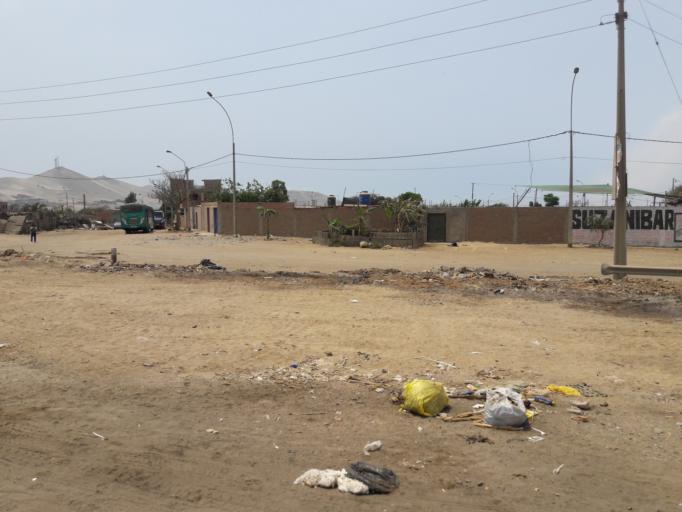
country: PE
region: Lima
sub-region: Lima
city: Santa Rosa
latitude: -11.7732
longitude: -77.1608
